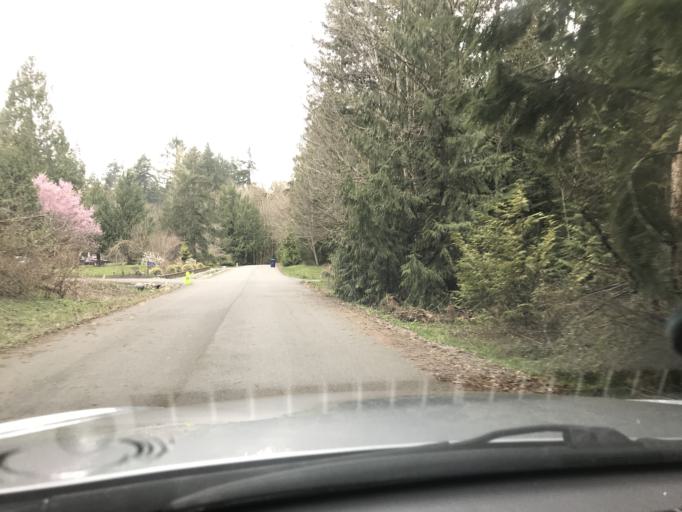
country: US
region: Washington
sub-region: King County
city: Union Hill-Novelty Hill
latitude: 47.7000
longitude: -122.0436
